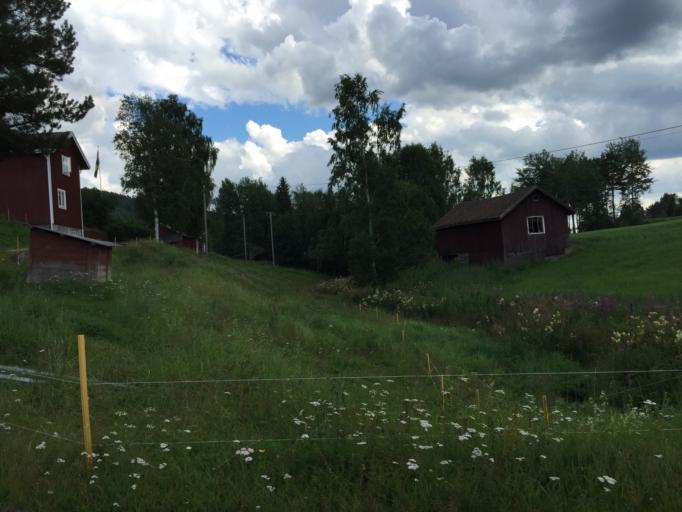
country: SE
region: Gaevleborg
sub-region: Ljusdals Kommun
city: Jaervsoe
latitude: 61.7461
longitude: 16.2703
